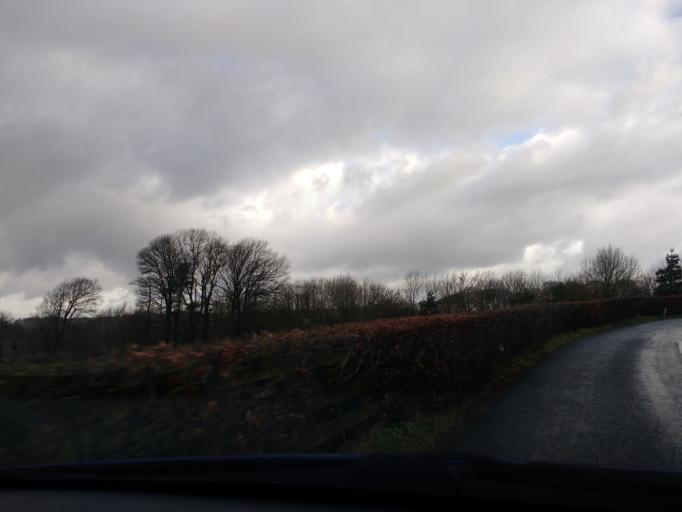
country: GB
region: England
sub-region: Lancashire
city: Caton
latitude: 54.0666
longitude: -2.7193
